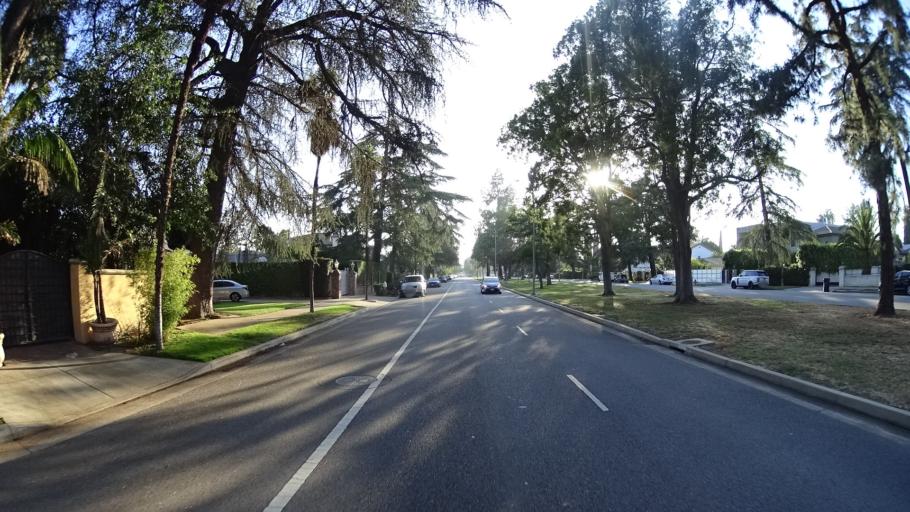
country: US
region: California
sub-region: Los Angeles County
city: Sherman Oaks
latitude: 34.1684
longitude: -118.4367
